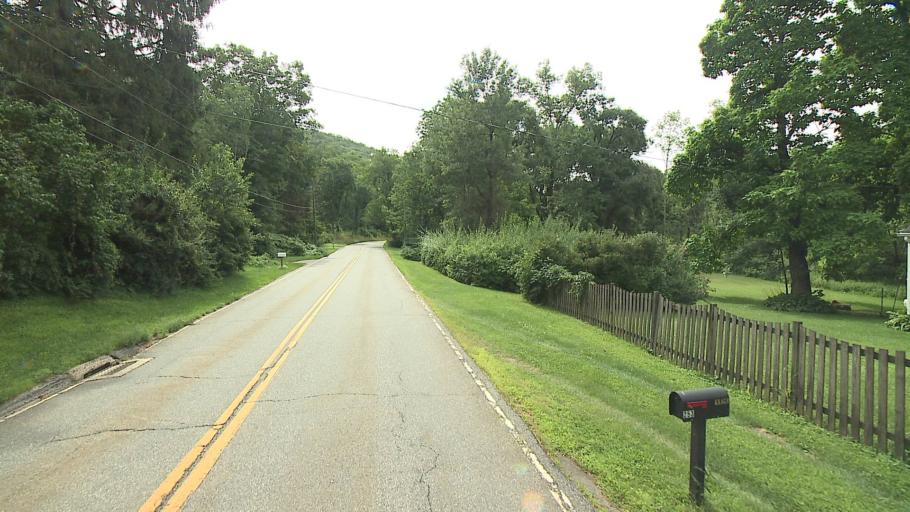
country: US
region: Connecticut
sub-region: Litchfield County
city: Kent
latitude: 41.7529
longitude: -73.5103
